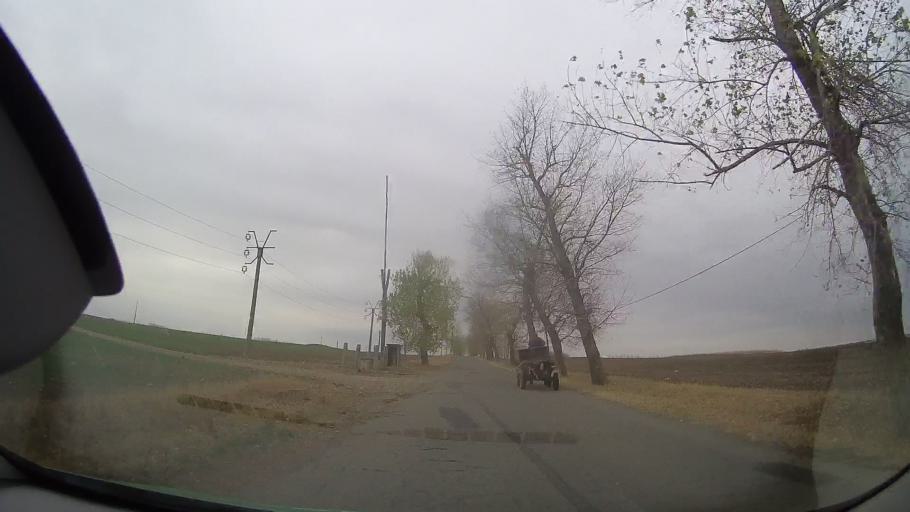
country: RO
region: Braila
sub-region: Comuna Ulmu
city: Jugureanu
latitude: 44.9418
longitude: 27.2504
